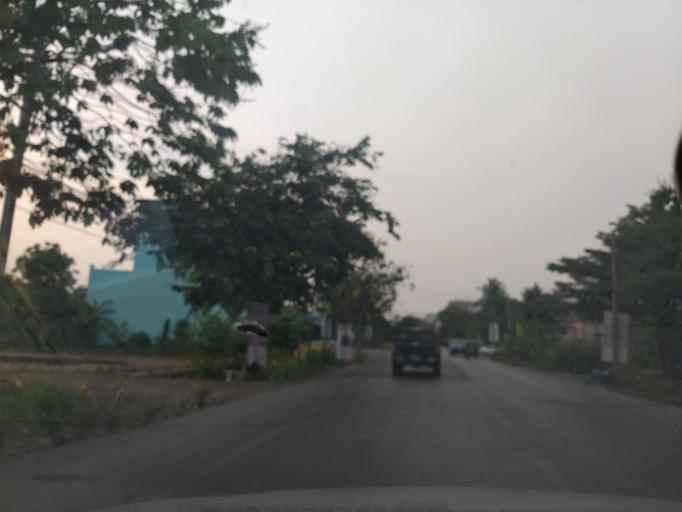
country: TH
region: Bangkok
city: Nong Chok
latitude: 13.8474
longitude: 100.8925
